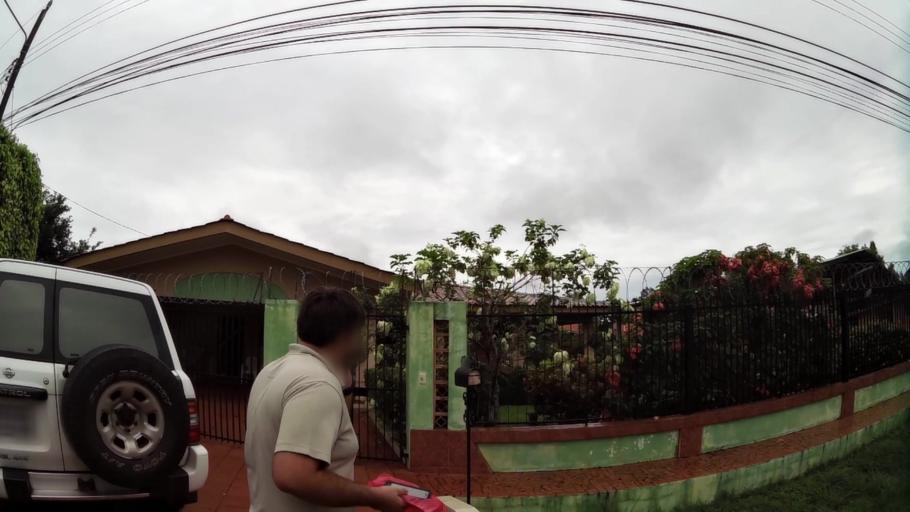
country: PA
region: Chiriqui
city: David
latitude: 8.4248
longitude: -82.4522
